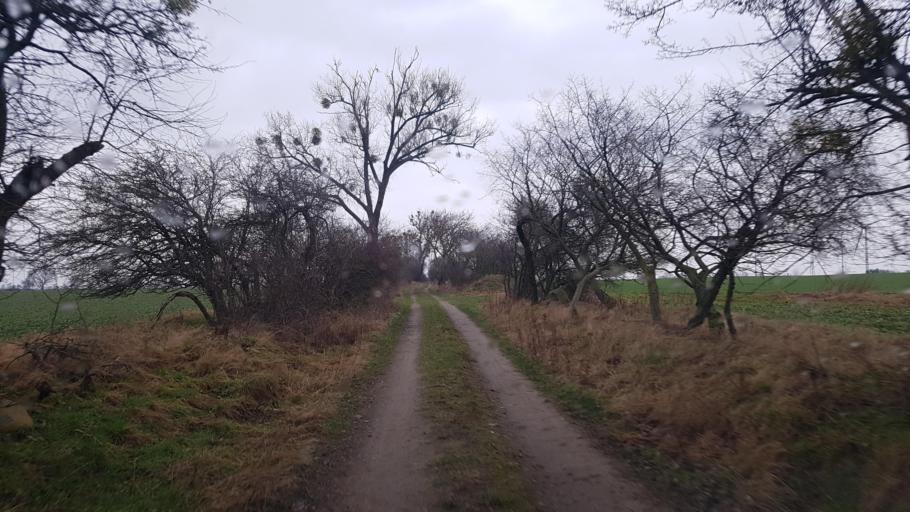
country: DE
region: Brandenburg
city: Zehdenick
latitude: 52.9507
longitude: 13.2551
